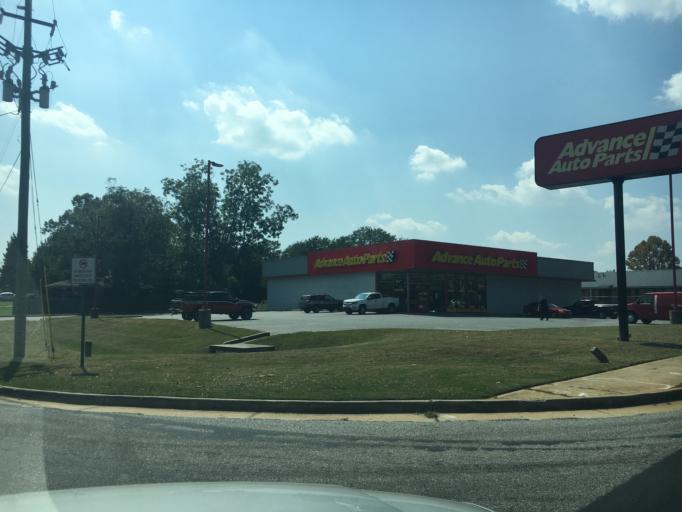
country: US
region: Georgia
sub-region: Hart County
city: Hartwell
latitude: 34.3539
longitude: -82.9192
